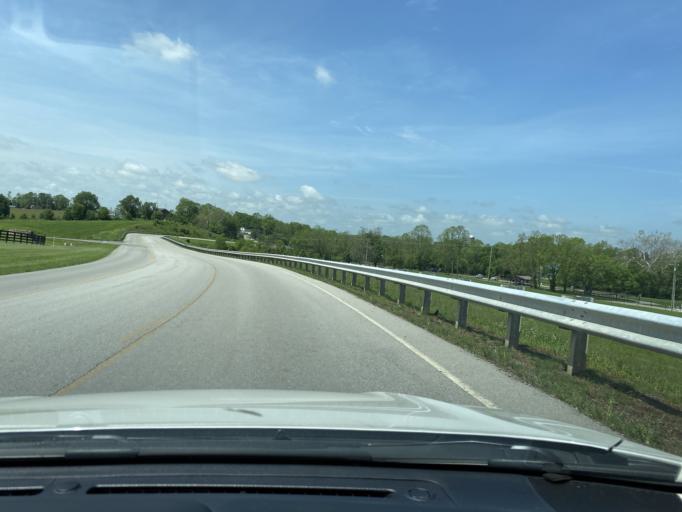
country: US
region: Kentucky
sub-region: Scott County
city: Georgetown
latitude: 38.2169
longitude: -84.6019
